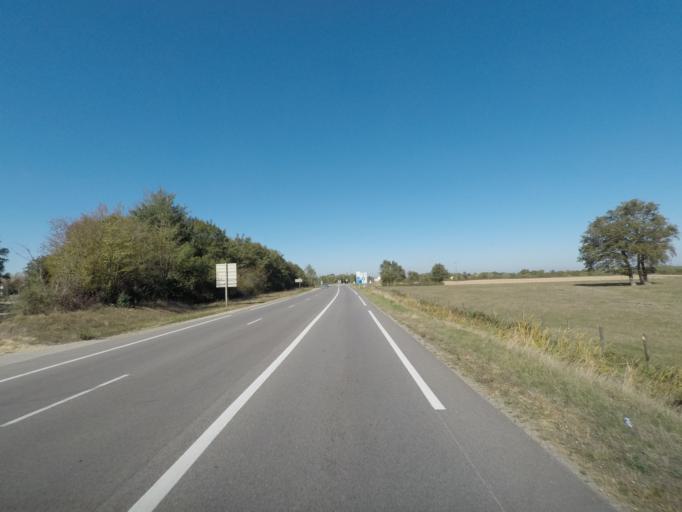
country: FR
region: Rhone-Alpes
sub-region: Departement de l'Ain
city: Attignat
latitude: 46.2576
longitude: 5.1785
